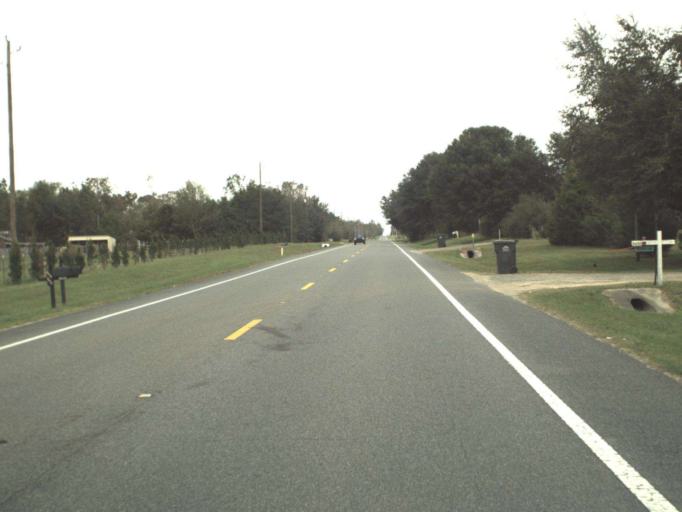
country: US
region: Florida
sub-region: Santa Rosa County
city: Point Baker
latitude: 30.7423
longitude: -87.0935
